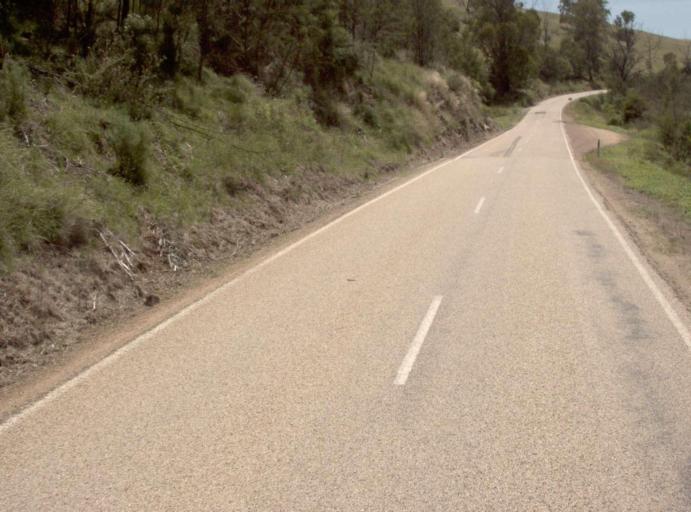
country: AU
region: Victoria
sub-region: East Gippsland
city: Bairnsdale
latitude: -37.5270
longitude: 147.8433
